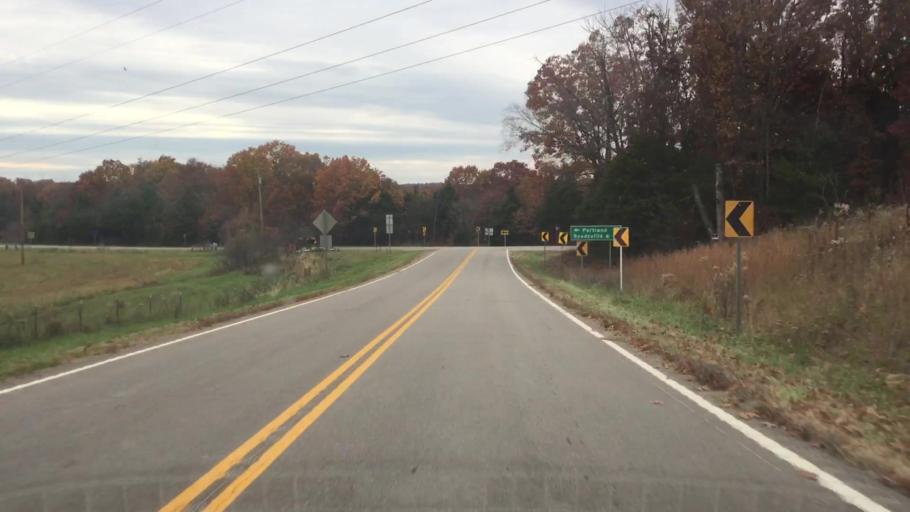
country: US
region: Missouri
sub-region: Gasconade County
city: Hermann
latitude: 38.7247
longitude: -91.7034
